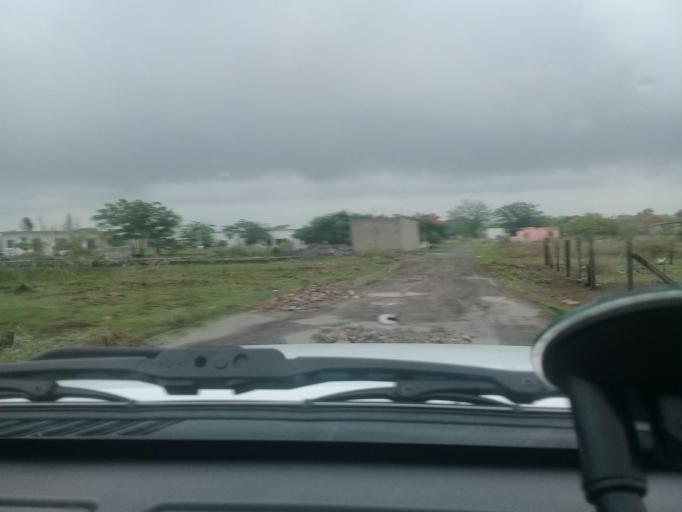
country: MX
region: Veracruz
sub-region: La Antigua
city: Nicolas Blanco (San Pancho)
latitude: 19.3376
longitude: -96.3630
